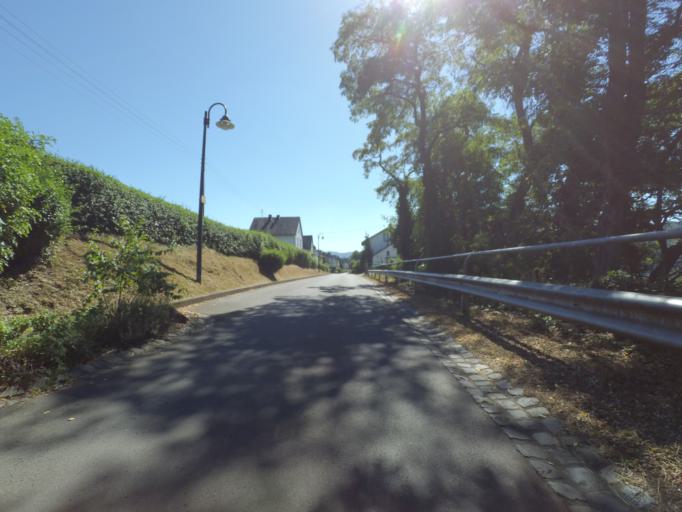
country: DE
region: Rheinland-Pfalz
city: Bullay
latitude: 50.0562
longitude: 7.1349
